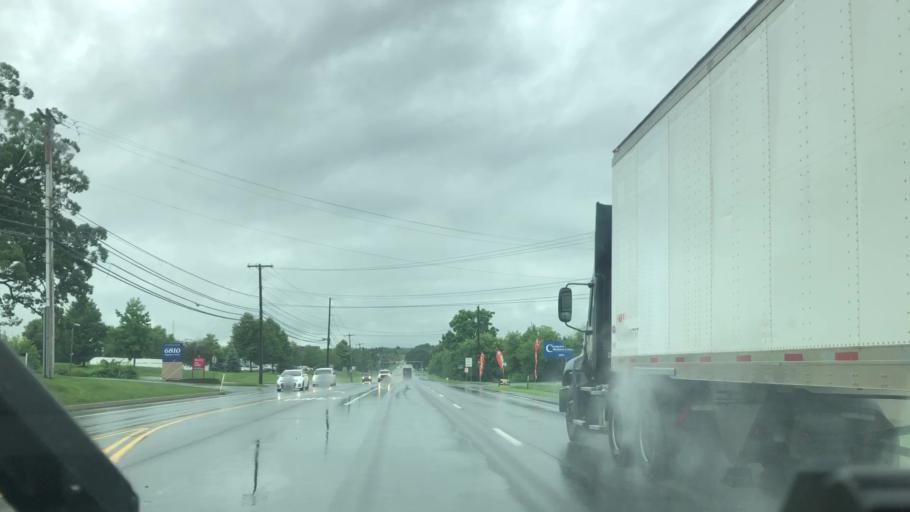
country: US
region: Pennsylvania
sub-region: Lehigh County
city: Trexlertown
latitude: 40.5887
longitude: -75.6062
